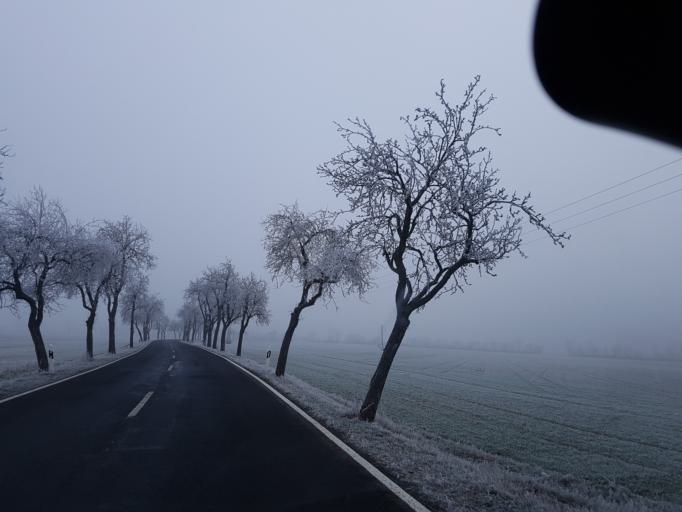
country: DE
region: Brandenburg
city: Muhlberg
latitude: 51.4266
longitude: 13.2508
